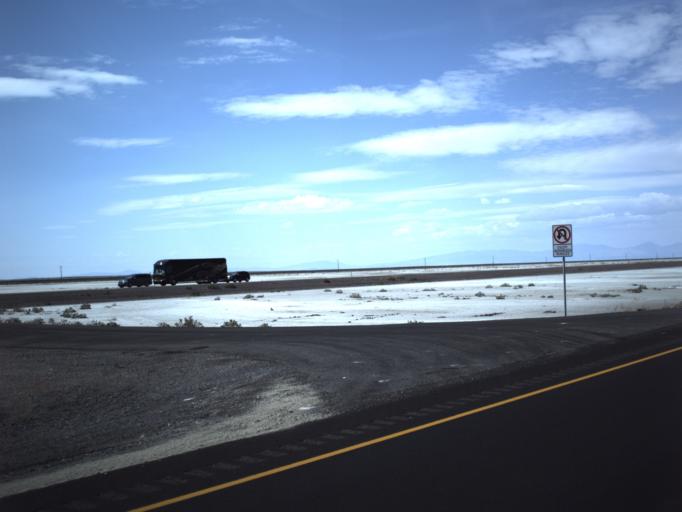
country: US
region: Utah
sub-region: Tooele County
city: Wendover
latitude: 40.7318
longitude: -113.4989
